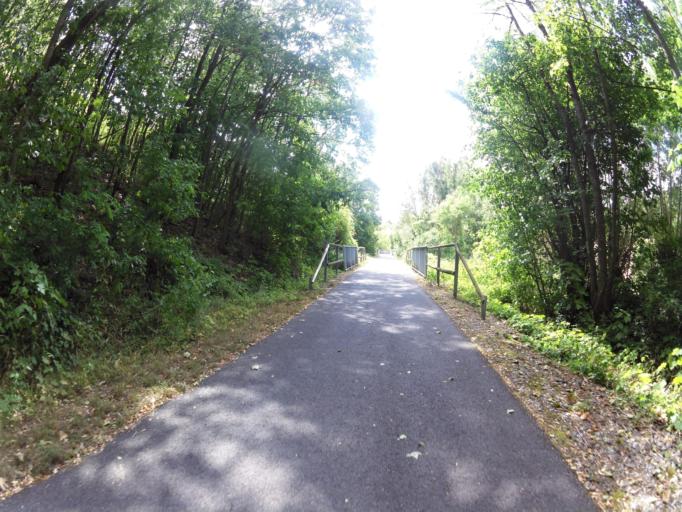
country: DE
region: Bavaria
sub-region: Regierungsbezirk Unterfranken
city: Ochsenfurt
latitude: 49.6542
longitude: 10.0289
